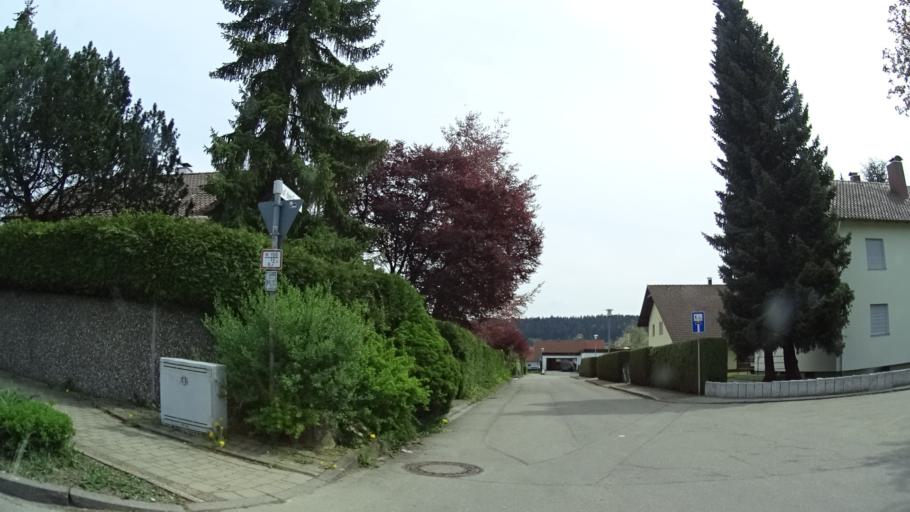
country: DE
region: Baden-Wuerttemberg
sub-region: Freiburg Region
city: Deisslingen
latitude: 48.1166
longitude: 8.6090
